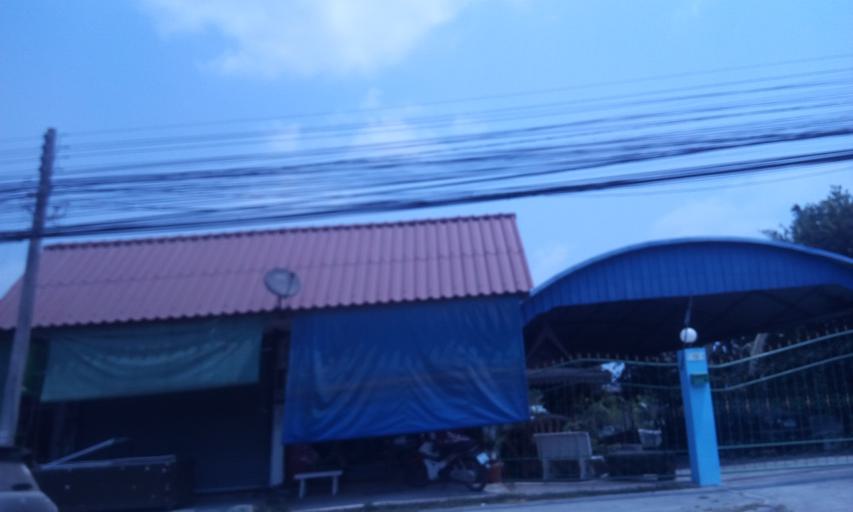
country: TH
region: Chachoengsao
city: Chachoengsao
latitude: 13.7032
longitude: 101.0916
